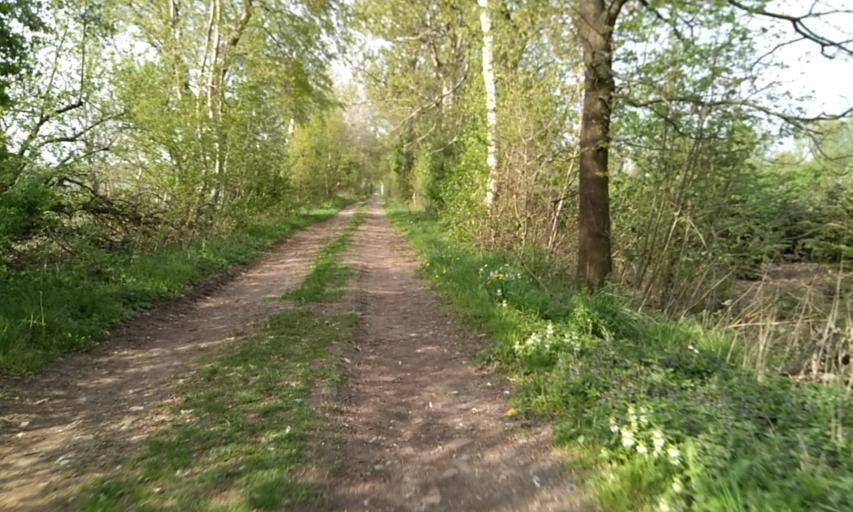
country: DE
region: Lower Saxony
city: Bliedersdorf
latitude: 53.4397
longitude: 9.5653
